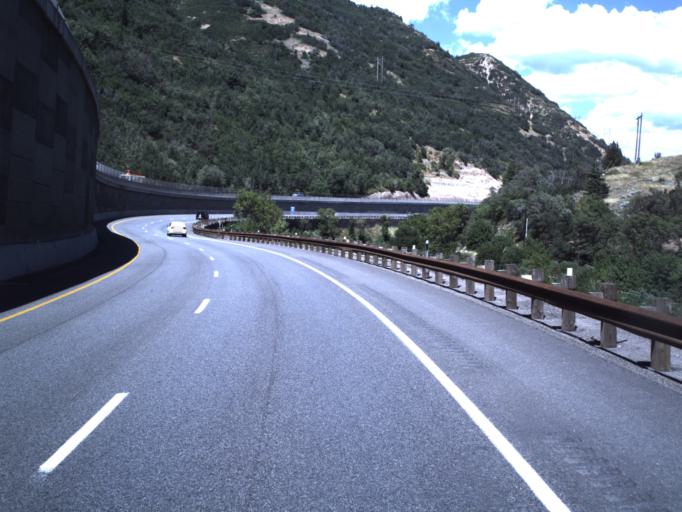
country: US
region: Utah
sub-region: Utah County
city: Orem
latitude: 40.3734
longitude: -111.5555
